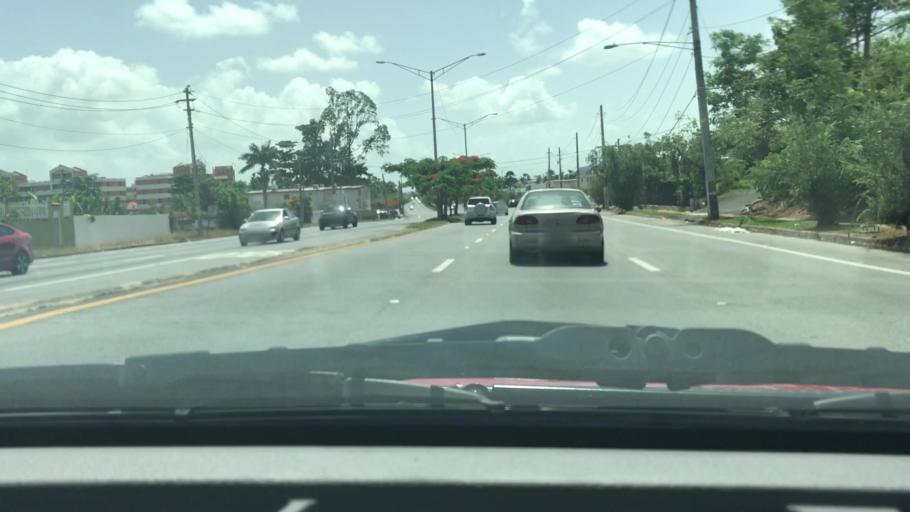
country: PR
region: Toa Alta
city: Pajaros
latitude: 18.3644
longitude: -66.1821
